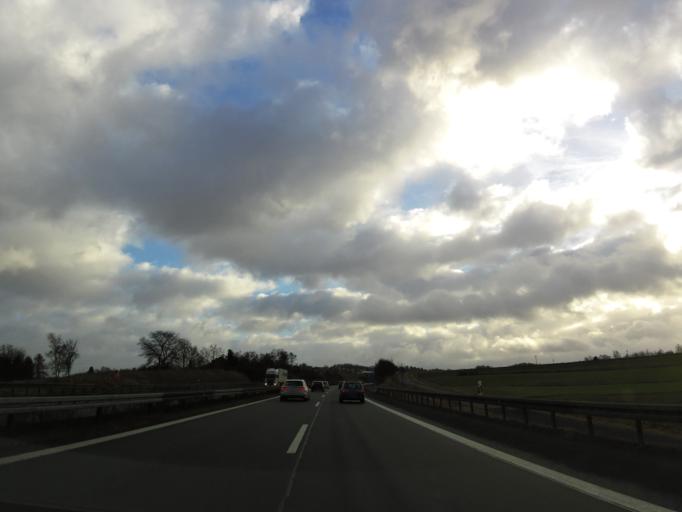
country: DE
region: Bavaria
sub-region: Upper Franconia
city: Thierstein
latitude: 50.1174
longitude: 12.0961
